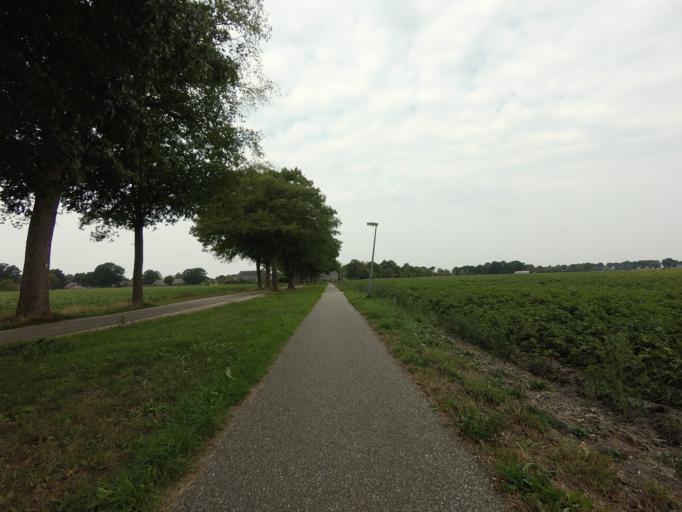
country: NL
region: Drenthe
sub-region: Gemeente Assen
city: Assen
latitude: 52.9930
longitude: 6.6369
